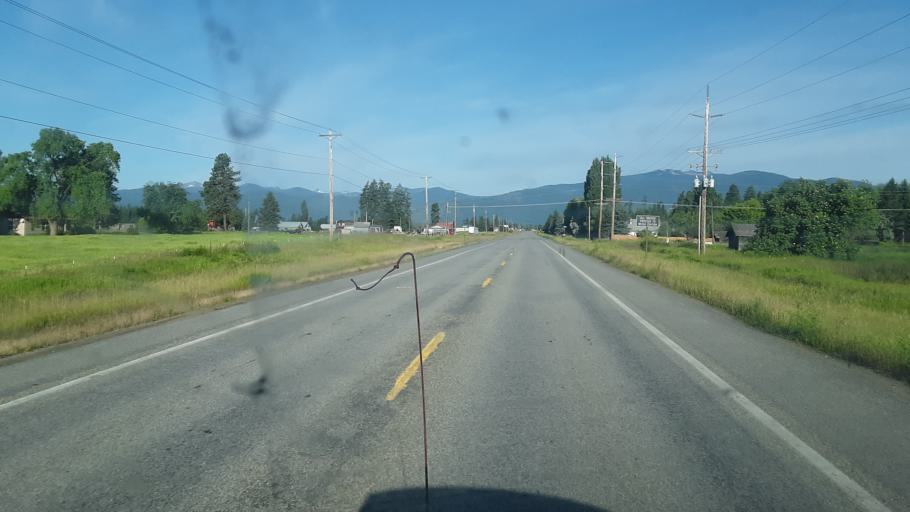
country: US
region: Idaho
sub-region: Boundary County
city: Bonners Ferry
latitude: 48.7315
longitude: -116.2736
